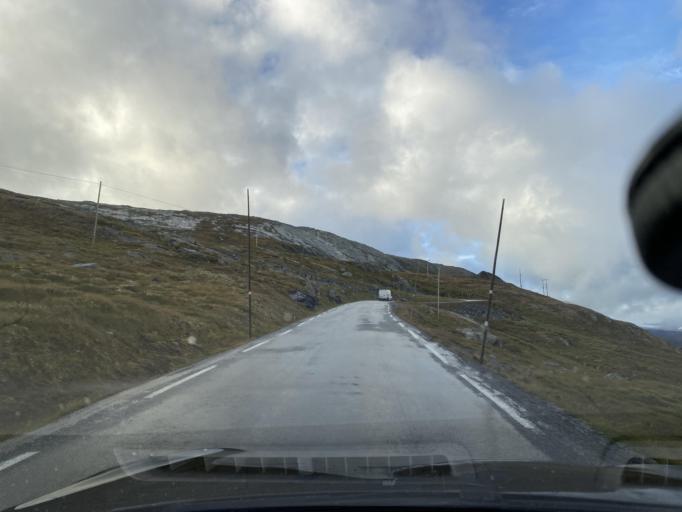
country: NO
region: Sogn og Fjordane
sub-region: Ardal
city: Farnes
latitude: 61.5713
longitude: 8.0299
